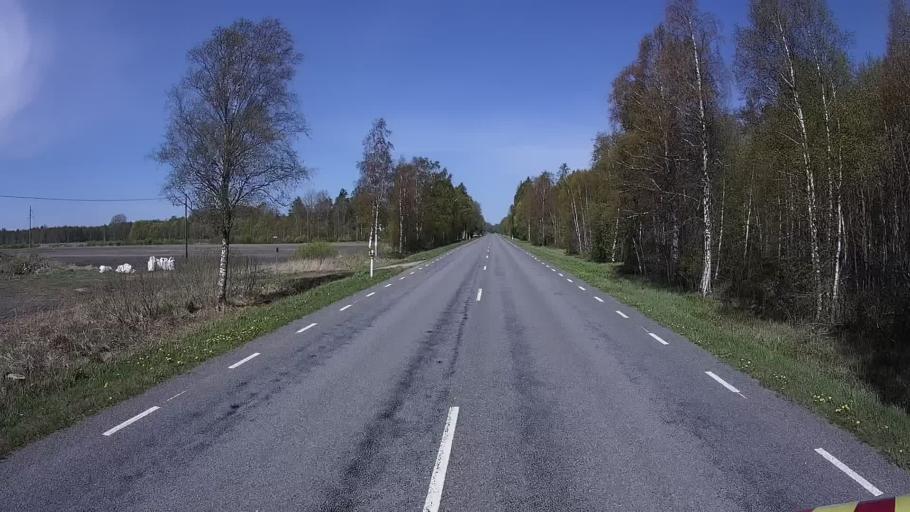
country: EE
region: Laeaene
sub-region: Lihula vald
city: Lihula
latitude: 58.6416
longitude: 23.8543
